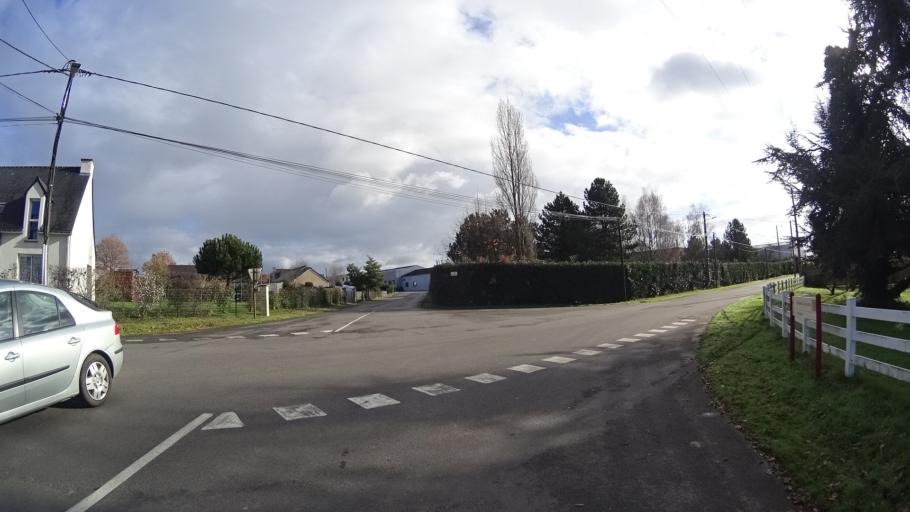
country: FR
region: Brittany
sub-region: Departement du Morbihan
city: Carentoir
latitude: 47.8124
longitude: -2.1333
